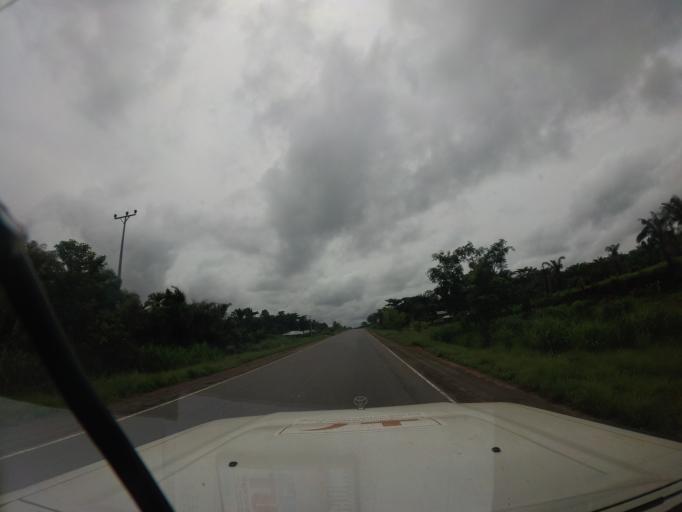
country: SL
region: Northern Province
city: Masingbi
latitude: 8.7525
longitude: -11.9675
